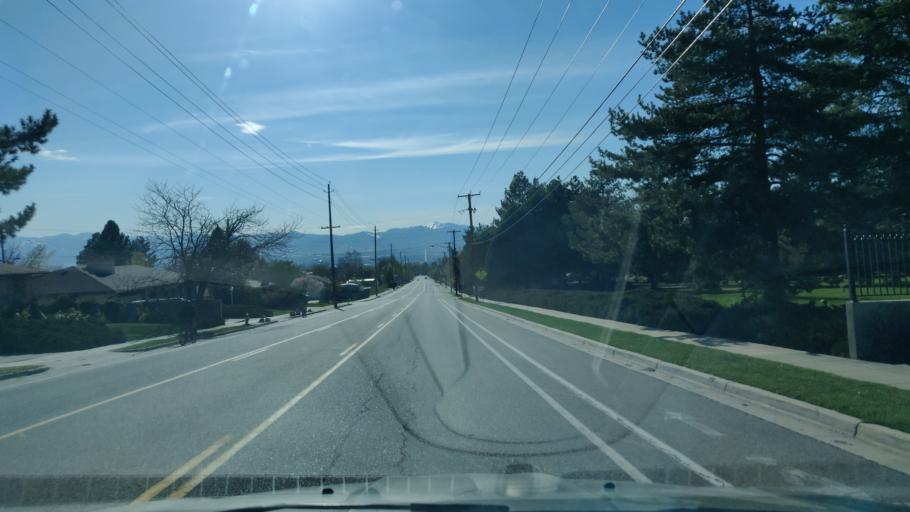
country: US
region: Utah
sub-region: Salt Lake County
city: Cottonwood Heights
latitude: 40.6095
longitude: -111.8036
